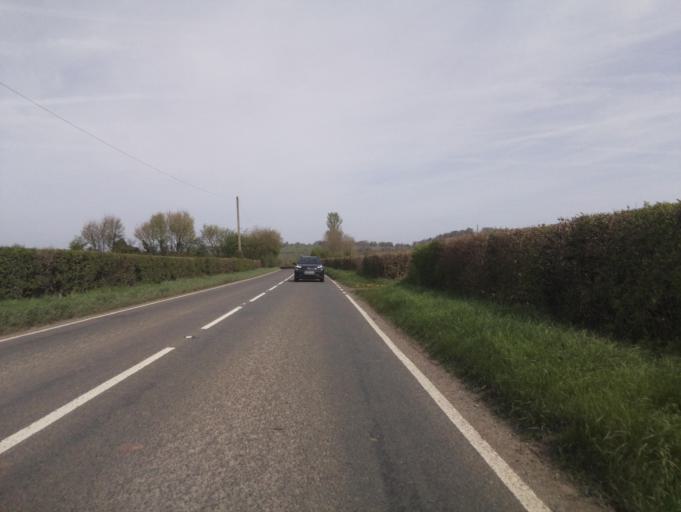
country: GB
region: England
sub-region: Somerset
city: Street
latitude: 51.0868
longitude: -2.7285
